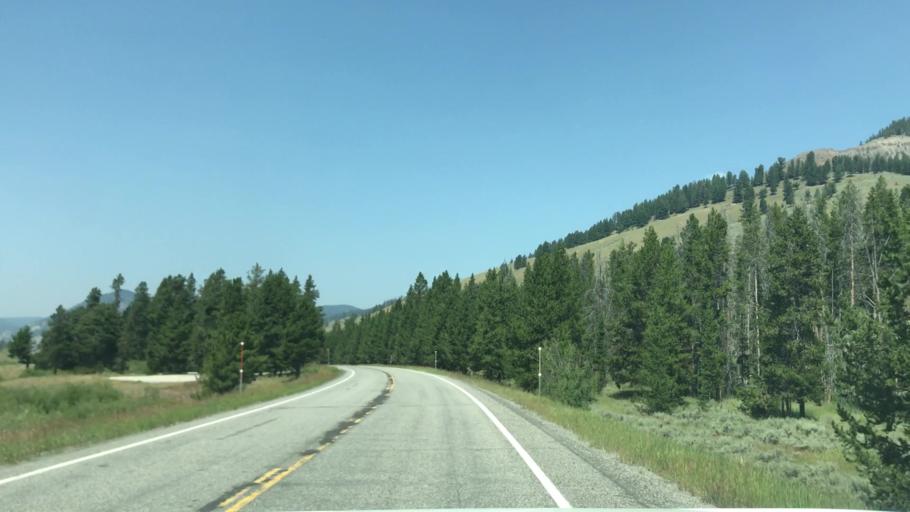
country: US
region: Montana
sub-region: Gallatin County
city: Big Sky
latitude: 45.0332
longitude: -111.1124
